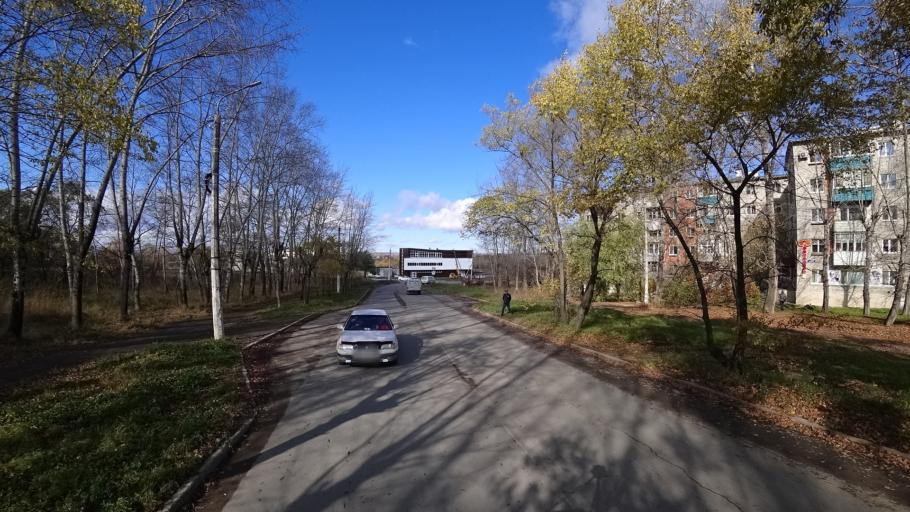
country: RU
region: Khabarovsk Krai
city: Amursk
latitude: 50.2226
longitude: 136.9025
